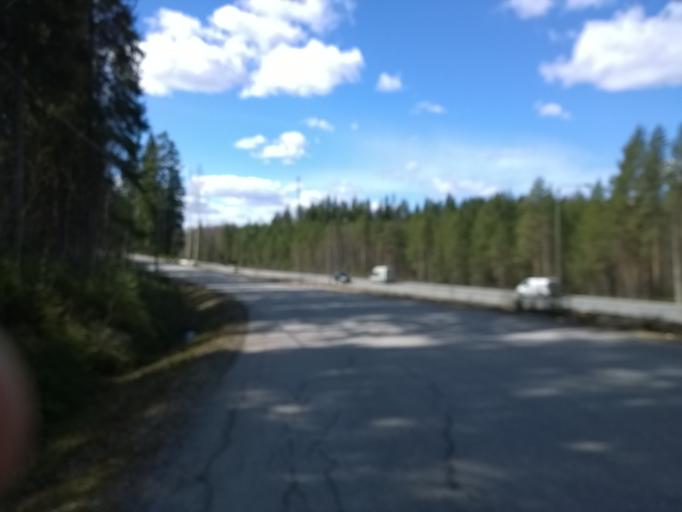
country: FI
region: Pirkanmaa
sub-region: Tampere
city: Tampere
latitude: 61.4353
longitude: 23.8411
